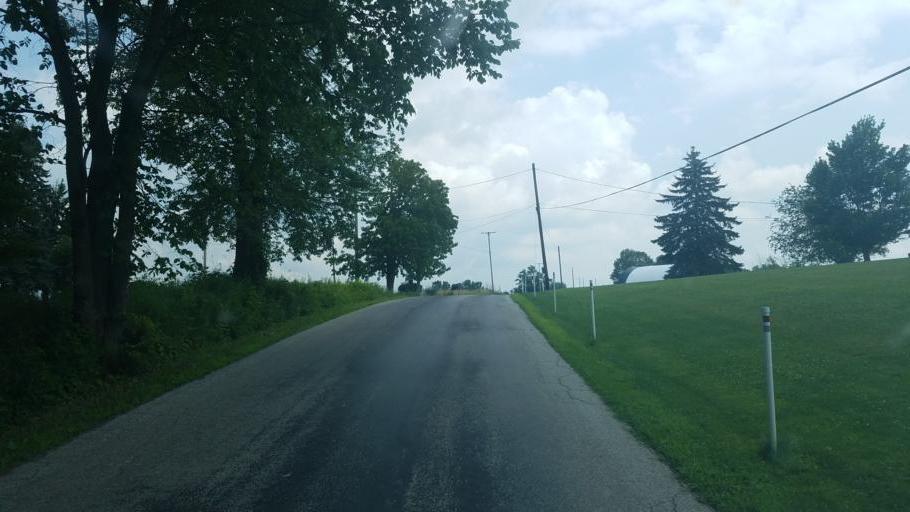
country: US
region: Ohio
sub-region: Richland County
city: Ontario
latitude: 40.8061
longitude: -82.6146
